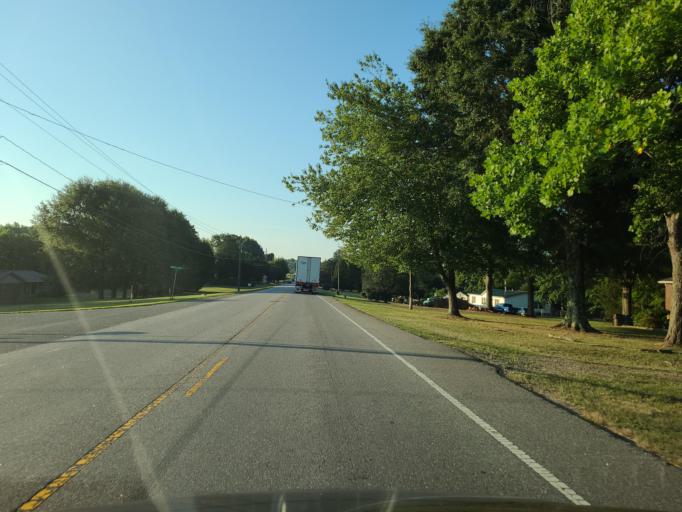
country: US
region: North Carolina
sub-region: Catawba County
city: Mountain View
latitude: 35.6312
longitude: -81.3794
